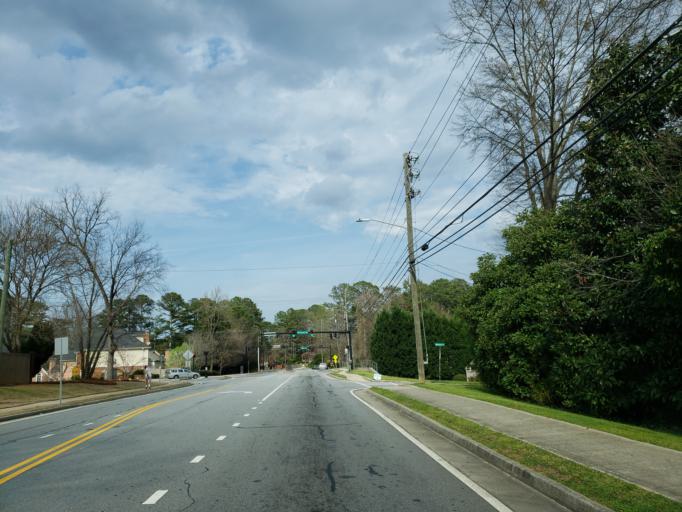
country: US
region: Georgia
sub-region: DeKalb County
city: Clarkston
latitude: 33.8332
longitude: -84.2730
